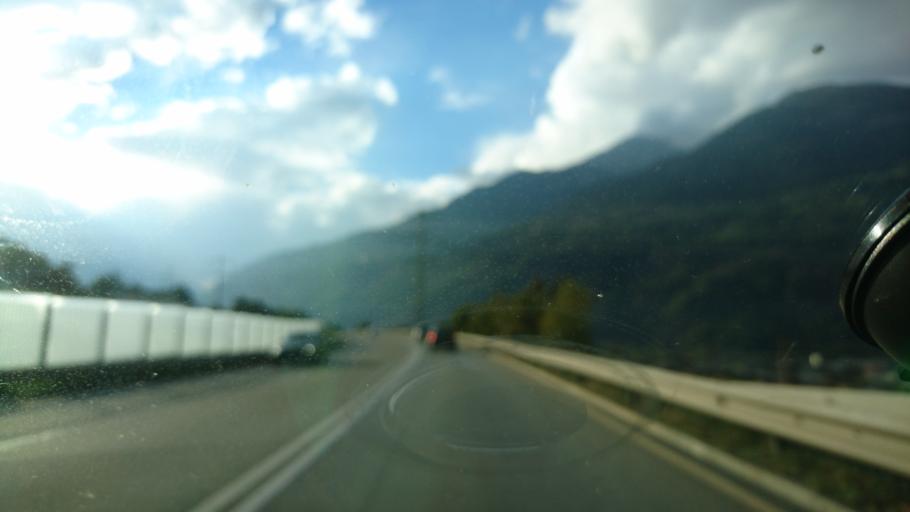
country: CH
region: Valais
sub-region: Brig District
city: Brig
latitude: 46.3079
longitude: 7.9921
